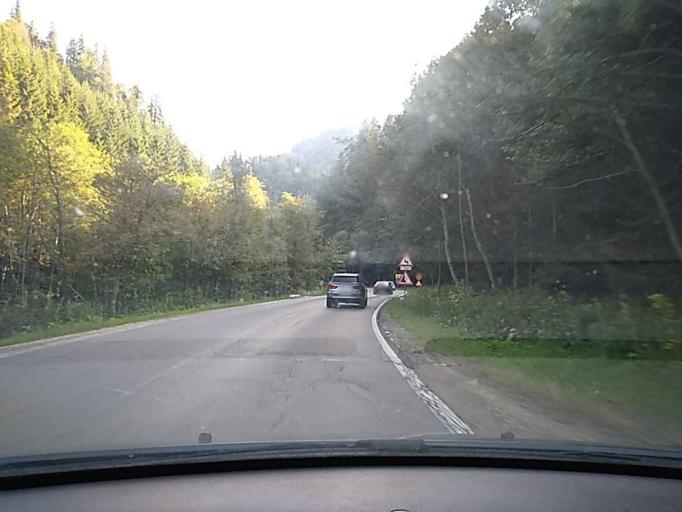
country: RO
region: Brasov
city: Crivina
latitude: 45.4785
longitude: 25.9199
